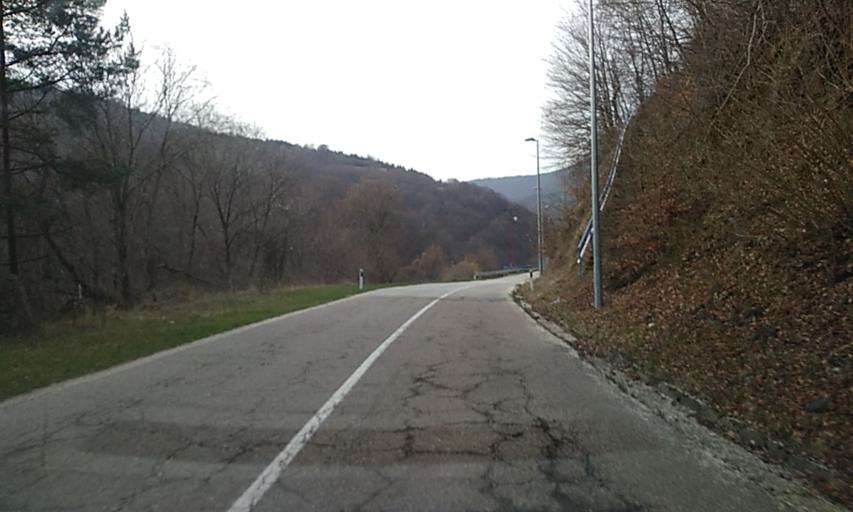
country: RS
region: Central Serbia
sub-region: Pcinjski Okrug
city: Bosilegrad
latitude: 42.5627
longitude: 22.3855
